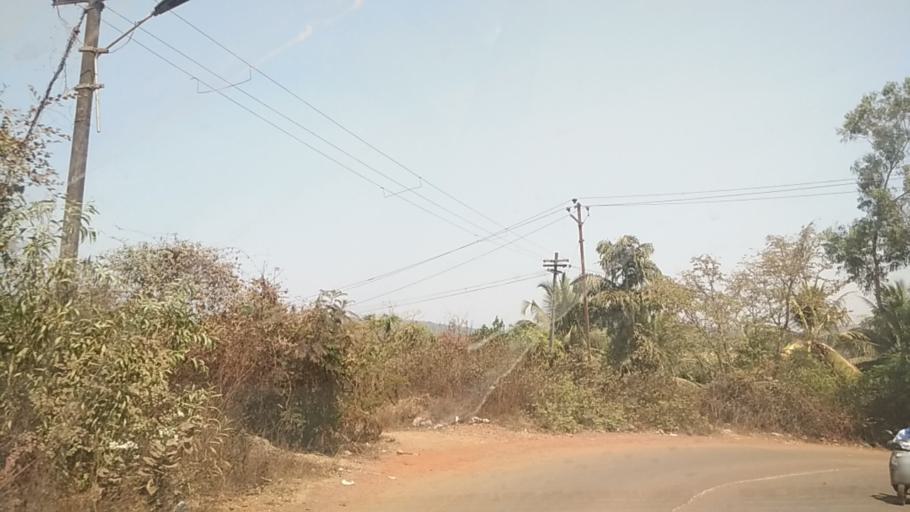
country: IN
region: Goa
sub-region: North Goa
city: Dicholi
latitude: 15.5861
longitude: 73.9421
